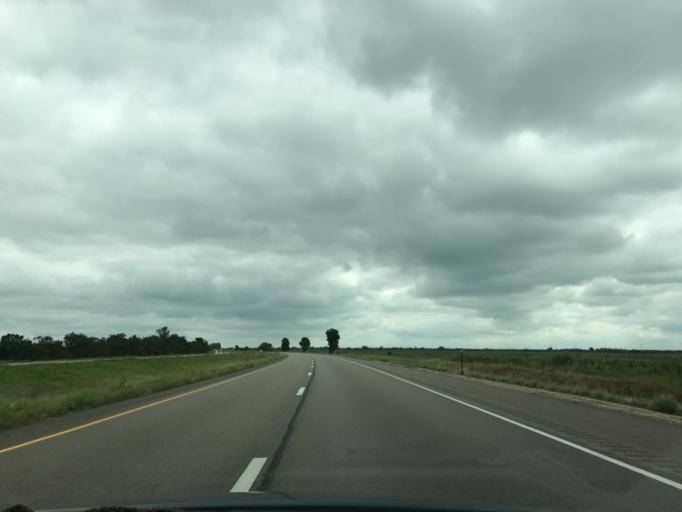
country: US
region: Illinois
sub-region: Bureau County
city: Princeton
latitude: 41.3874
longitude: -89.5468
